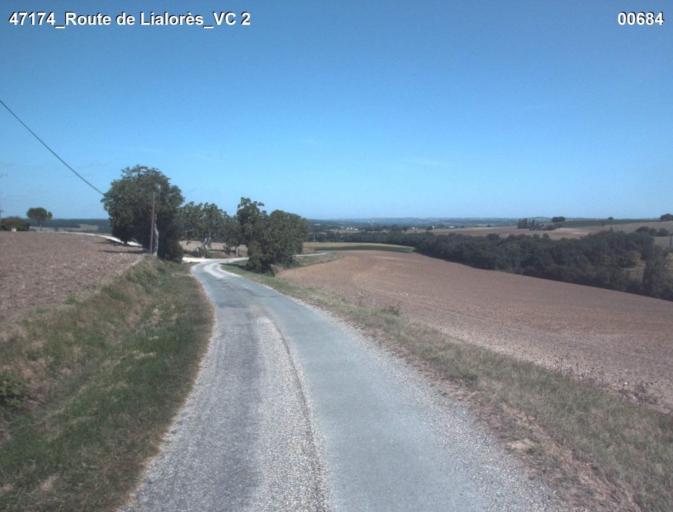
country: FR
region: Midi-Pyrenees
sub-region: Departement du Gers
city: Condom
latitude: 44.0127
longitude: 0.3788
